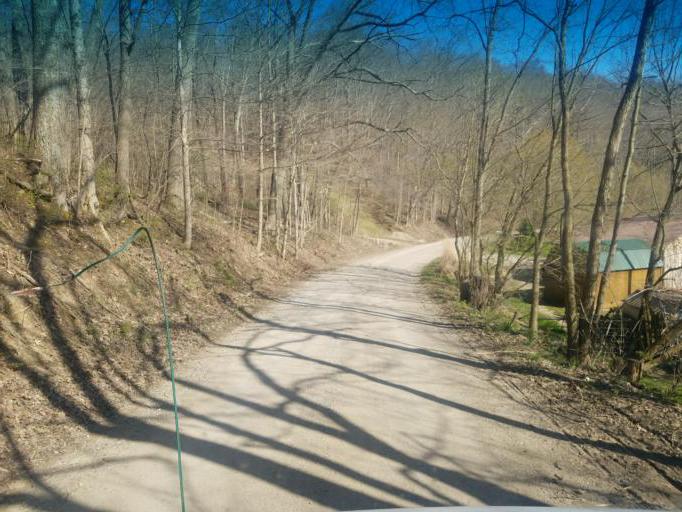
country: US
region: Ohio
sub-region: Muskingum County
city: Frazeysburg
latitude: 40.2245
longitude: -82.1803
